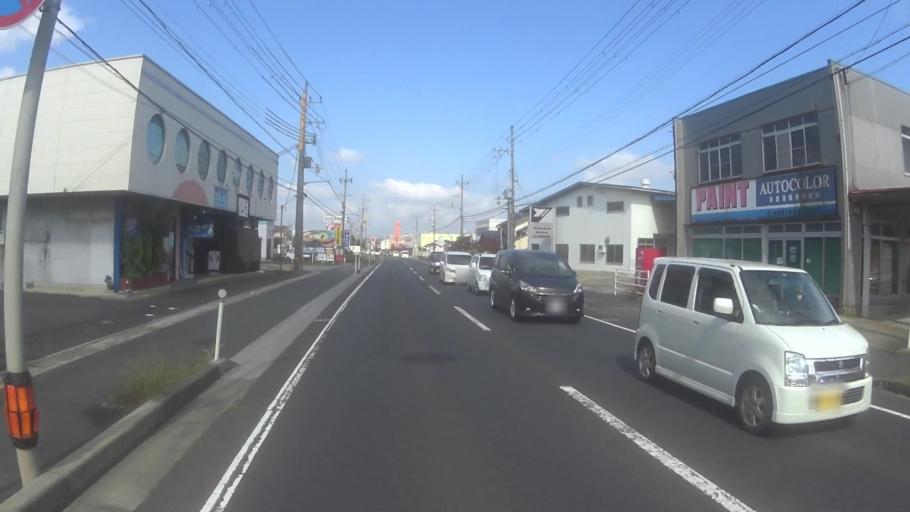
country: JP
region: Kyoto
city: Miyazu
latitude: 35.5925
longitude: 135.0927
